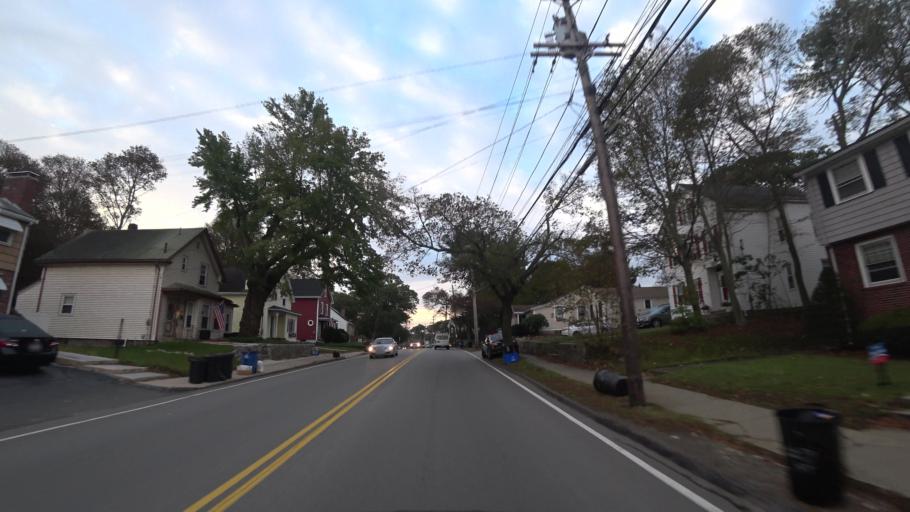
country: US
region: Massachusetts
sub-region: Essex County
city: Saugus
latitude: 42.4593
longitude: -71.0101
